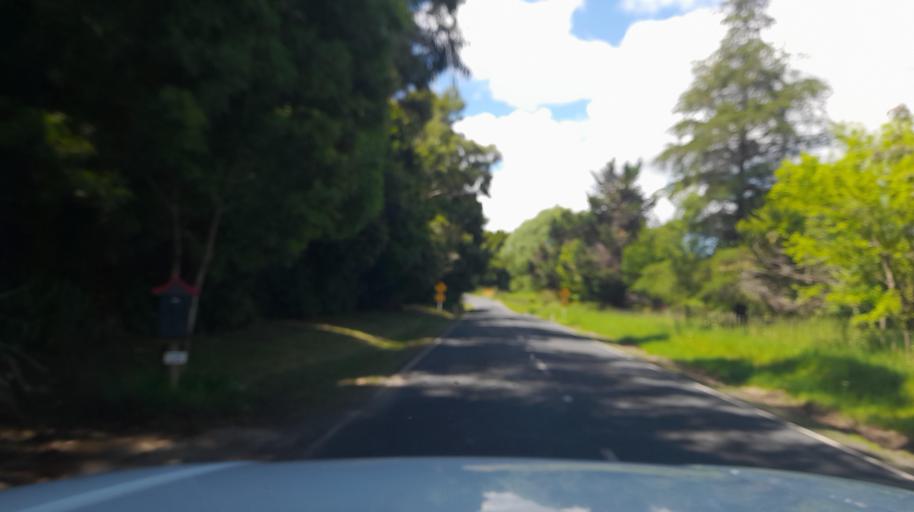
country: NZ
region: Northland
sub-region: Far North District
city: Taipa
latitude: -35.0942
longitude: 173.4967
